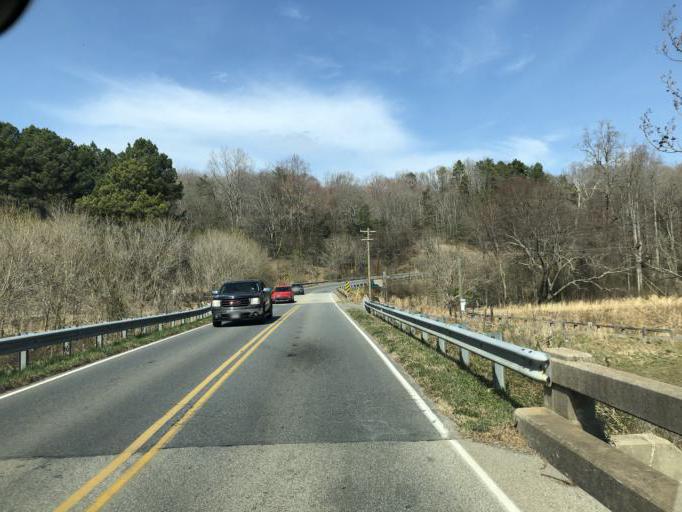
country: US
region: North Carolina
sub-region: Gaston County
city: Ranlo
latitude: 35.3089
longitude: -81.1068
